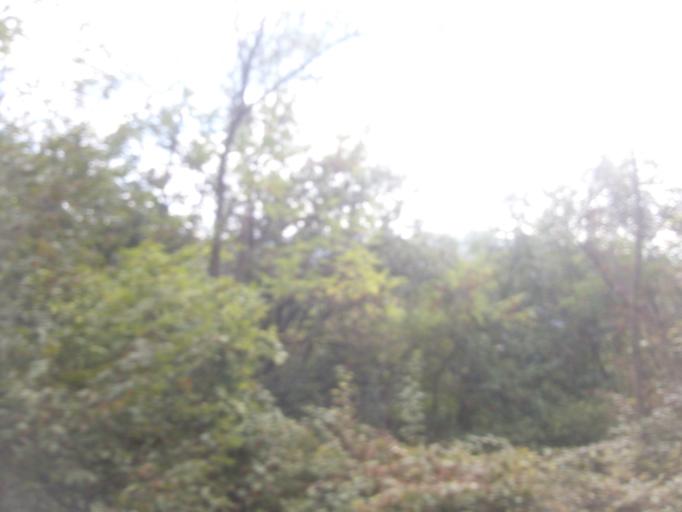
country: IT
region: Liguria
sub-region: Provincia di Genova
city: Piccarello
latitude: 44.4611
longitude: 8.9501
